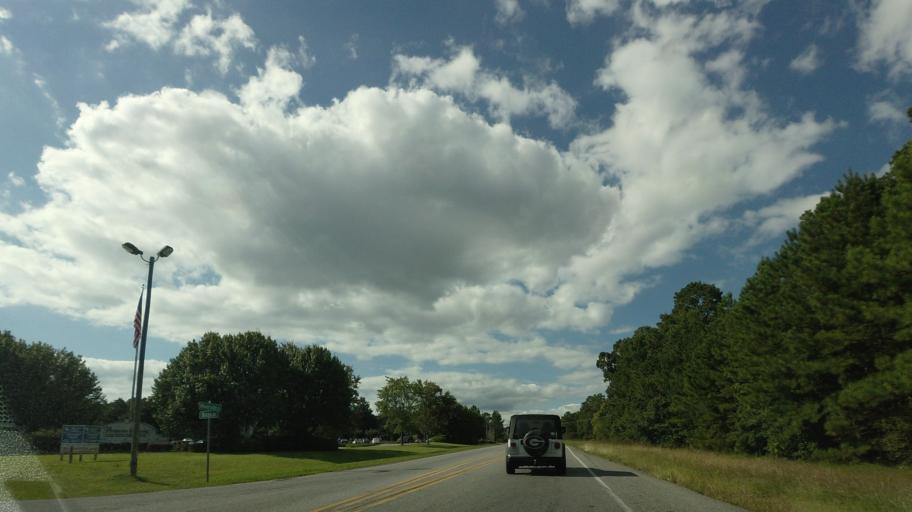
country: US
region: Georgia
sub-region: Bibb County
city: Macon
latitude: 32.9367
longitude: -83.7173
